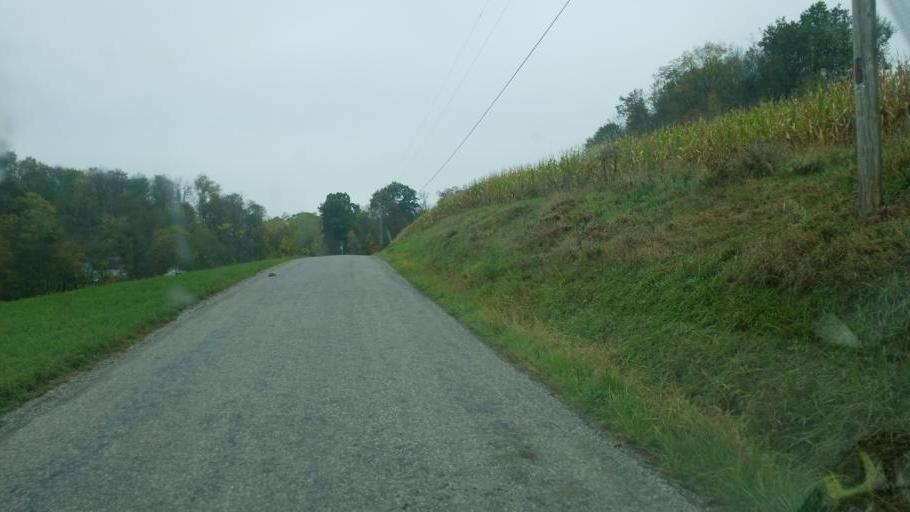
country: US
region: Ohio
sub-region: Tuscarawas County
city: Sugarcreek
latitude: 40.5730
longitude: -81.7016
